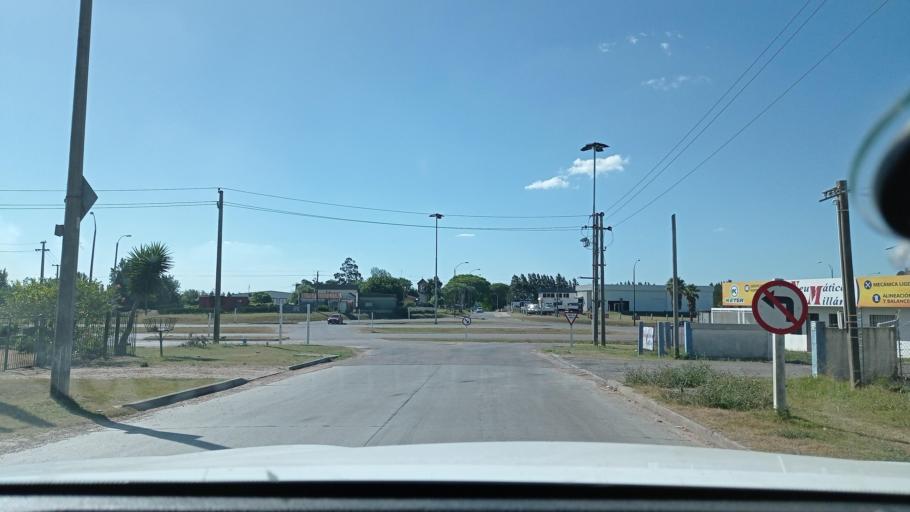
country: UY
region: Canelones
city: La Paz
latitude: -34.7679
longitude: -56.2656
